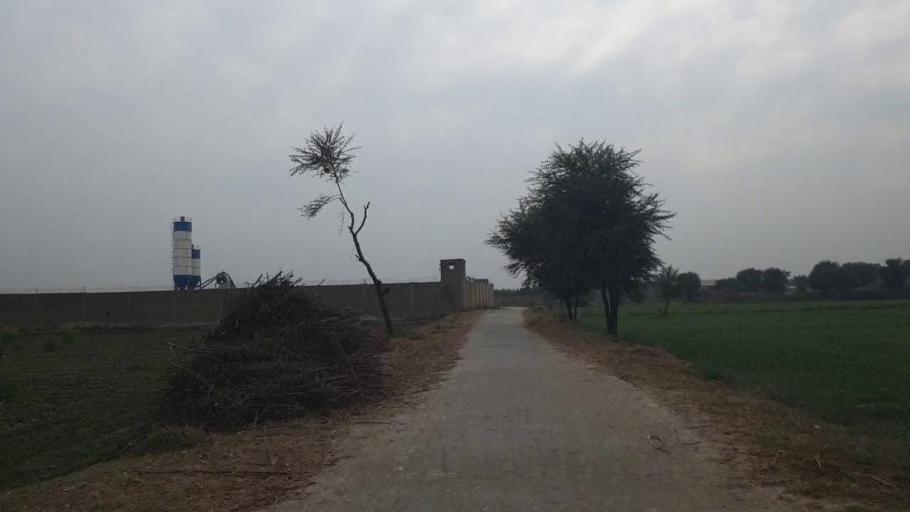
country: PK
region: Sindh
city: Shahdadpur
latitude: 25.9379
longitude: 68.7012
